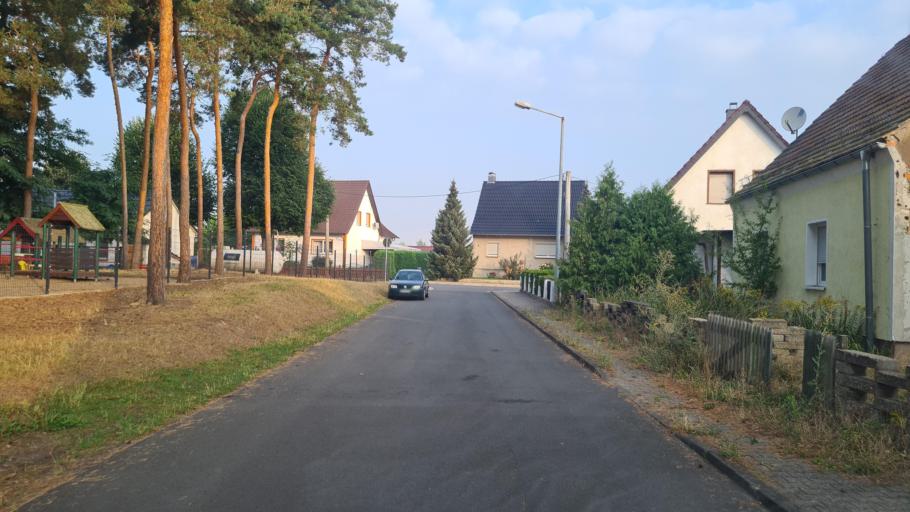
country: DE
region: Saxony
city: Beilrode
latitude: 51.5827
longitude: 13.0450
